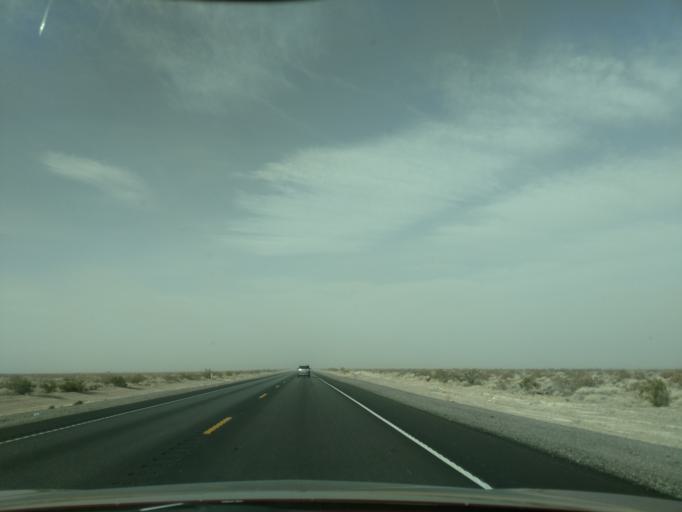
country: US
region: Nevada
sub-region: Nye County
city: Beatty
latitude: 36.6348
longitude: -116.3639
